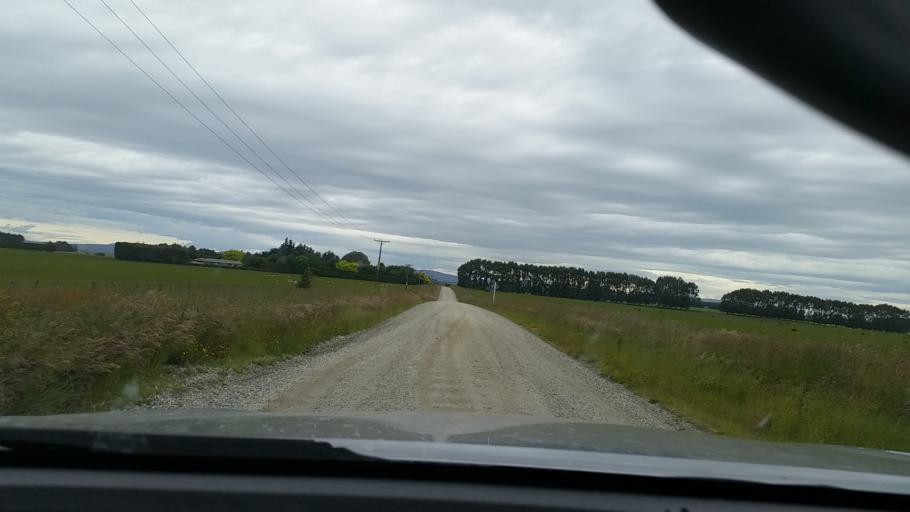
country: NZ
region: Southland
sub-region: Gore District
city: Gore
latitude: -46.3073
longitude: 168.7328
